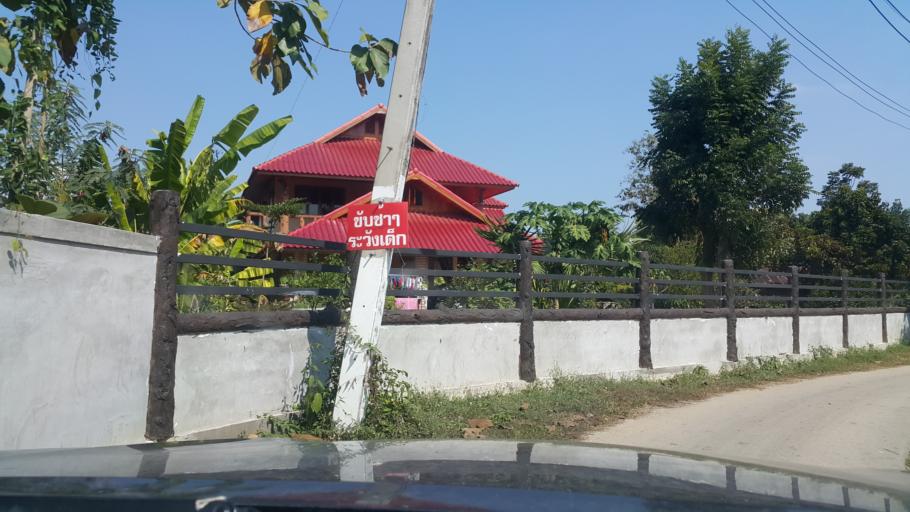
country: TH
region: Sukhothai
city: Thung Saliam
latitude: 17.3197
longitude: 99.5742
